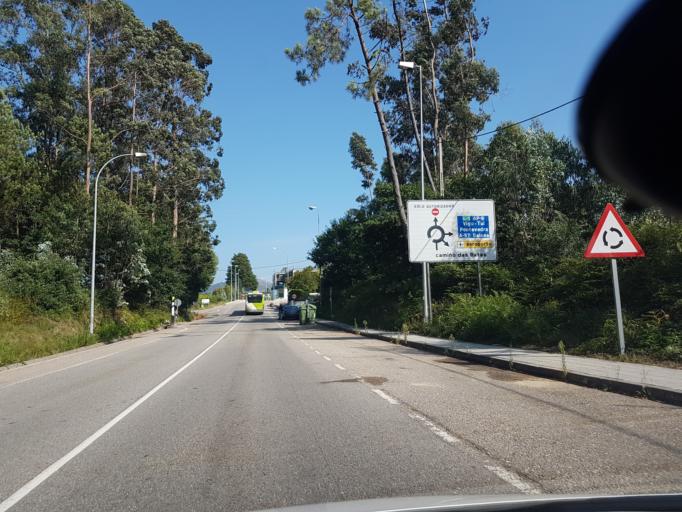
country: ES
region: Galicia
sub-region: Provincia de Pontevedra
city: Redondela
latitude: 42.2290
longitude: -8.6347
